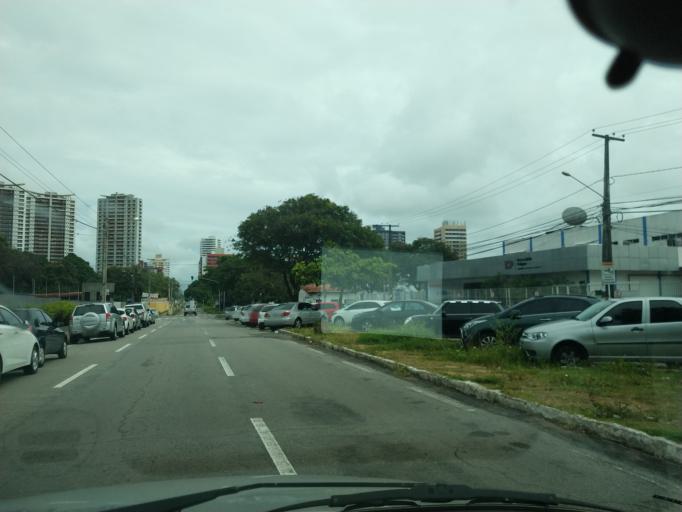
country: BR
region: Rio Grande do Norte
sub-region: Natal
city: Natal
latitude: -5.8149
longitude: -35.2161
